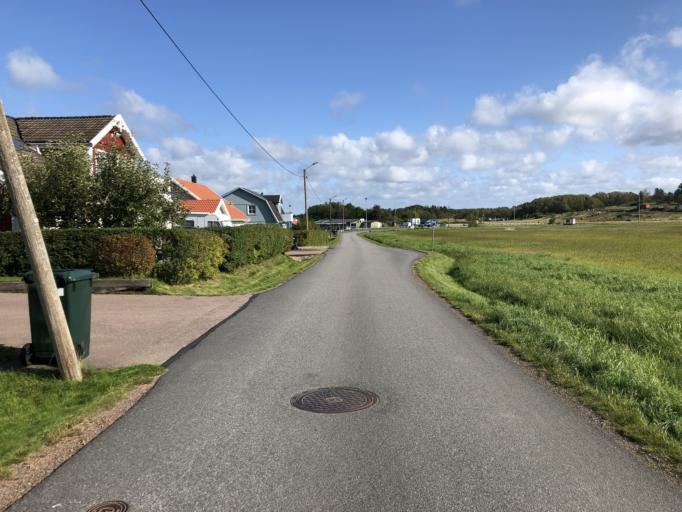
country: SE
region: Vaestra Goetaland
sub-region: Goteborg
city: Torslanda
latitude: 57.7492
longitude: 11.8253
